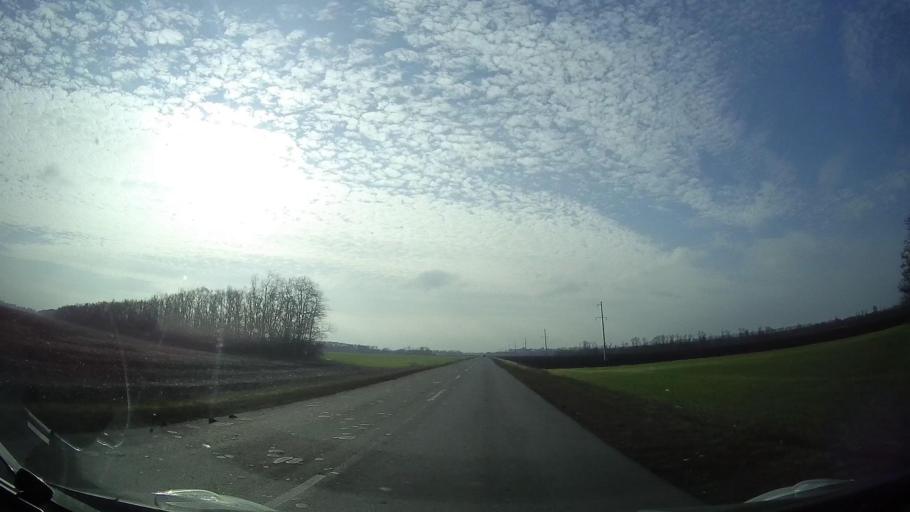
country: RU
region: Rostov
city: Mechetinskaya
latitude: 46.8072
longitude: 40.5292
